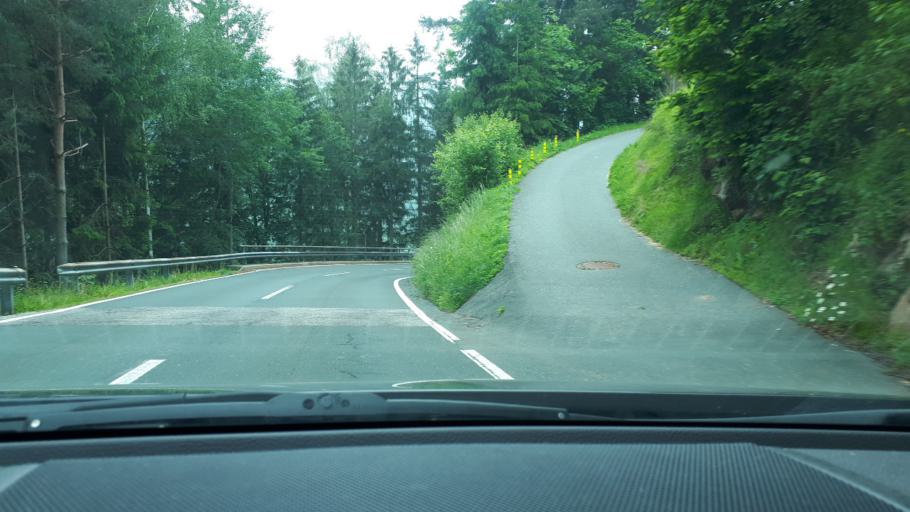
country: AT
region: Carinthia
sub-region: Politischer Bezirk Wolfsberg
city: Preitenegg
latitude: 46.9320
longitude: 14.8923
